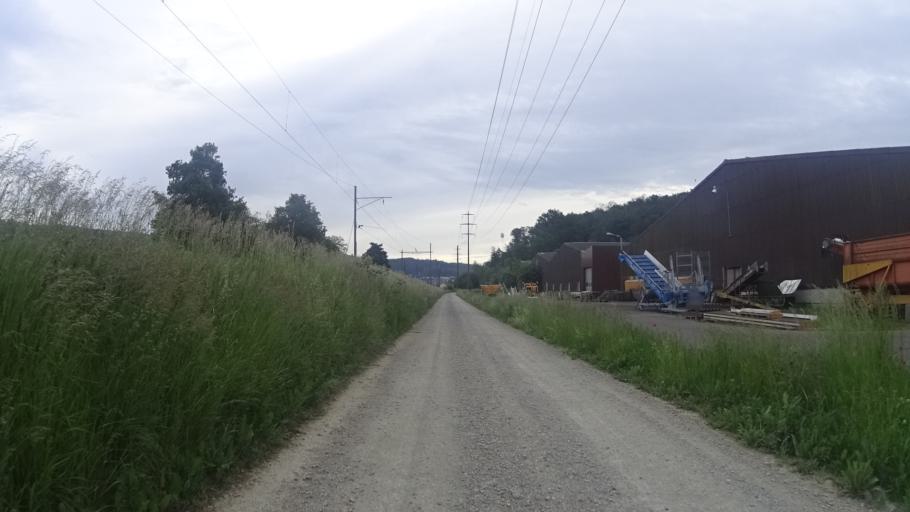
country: DE
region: Baden-Wuerttemberg
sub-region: Freiburg Region
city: Waldshut-Tiengen
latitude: 47.6082
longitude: 8.1950
